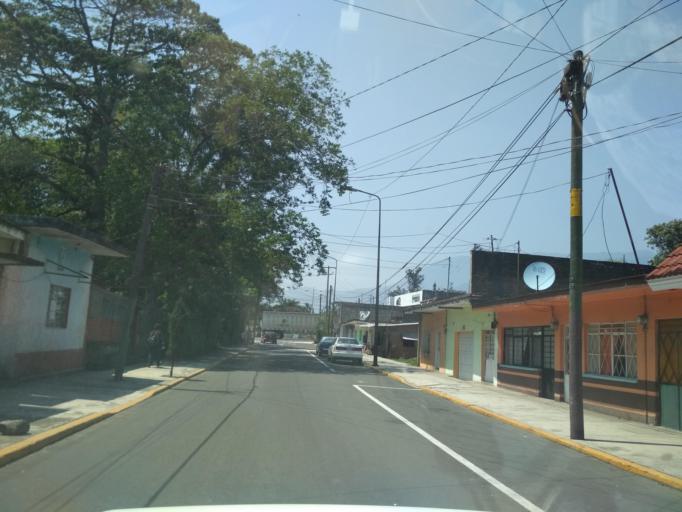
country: MX
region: Veracruz
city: Orizaba
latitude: 18.8356
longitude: -97.1080
